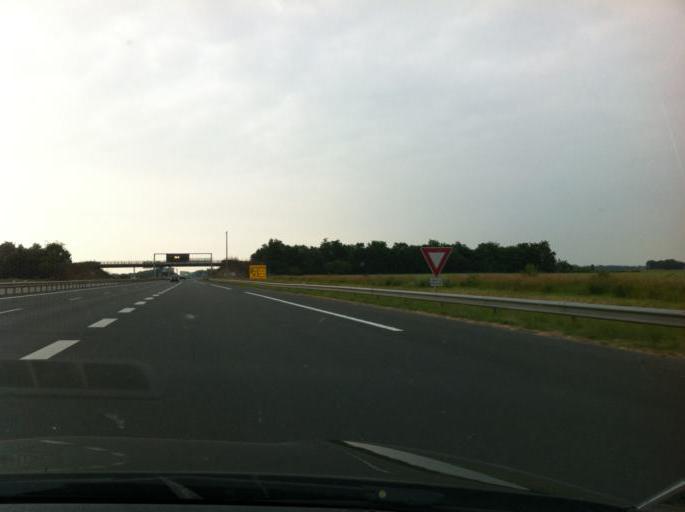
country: FR
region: Ile-de-France
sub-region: Departement de Seine-et-Marne
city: Vert-Saint-Denis
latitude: 48.5988
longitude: 2.6350
